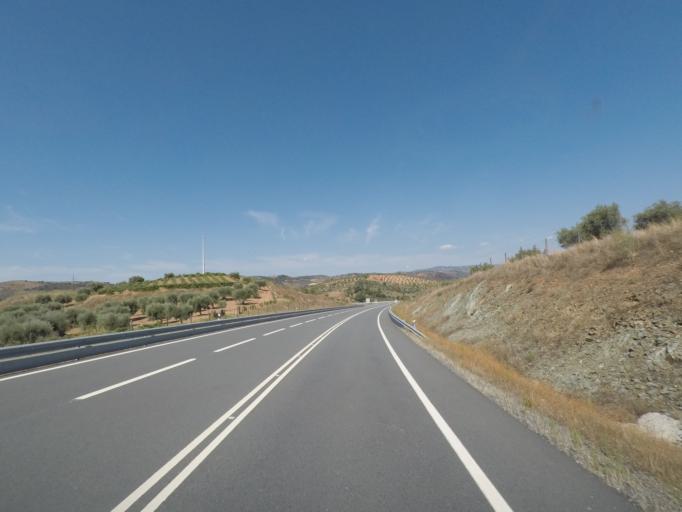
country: PT
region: Braganca
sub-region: Alfandega da Fe
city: Alfandega da Fe
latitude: 41.3052
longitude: -6.9054
